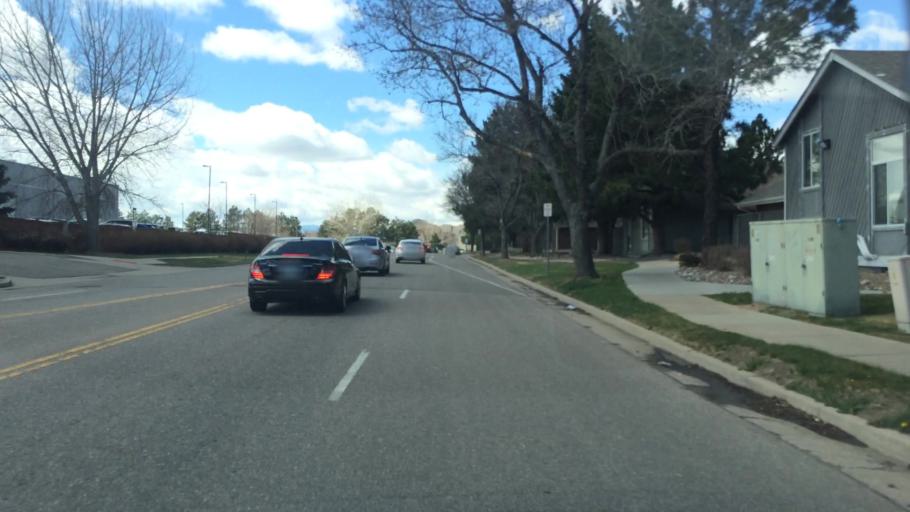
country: US
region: Colorado
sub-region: Arapahoe County
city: Centennial
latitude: 39.5972
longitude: -104.8703
